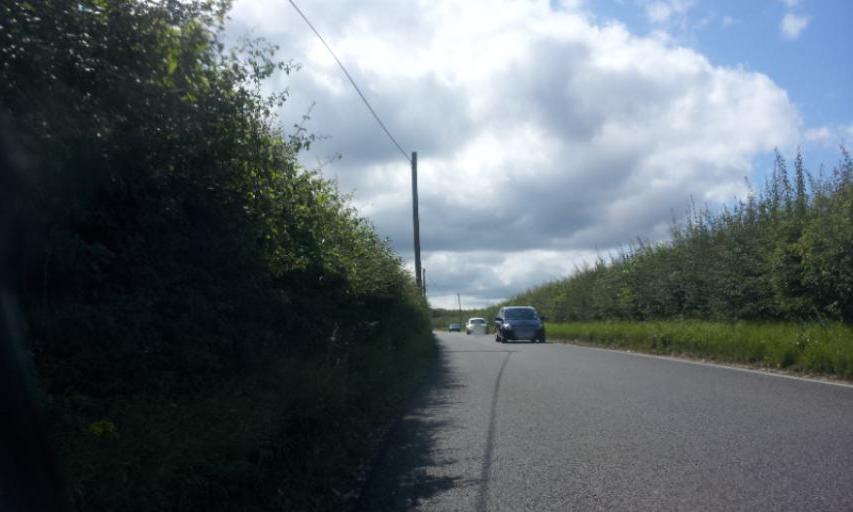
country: GB
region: England
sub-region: Kent
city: Boxley
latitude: 51.3140
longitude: 0.5507
